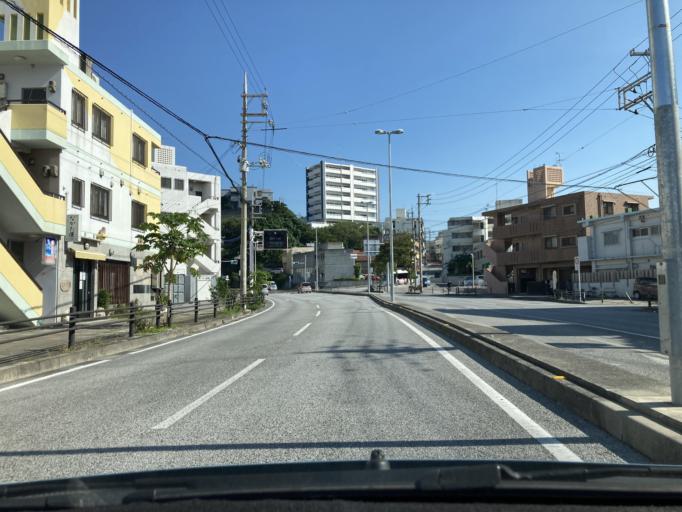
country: JP
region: Okinawa
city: Naha-shi
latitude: 26.2036
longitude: 127.7062
